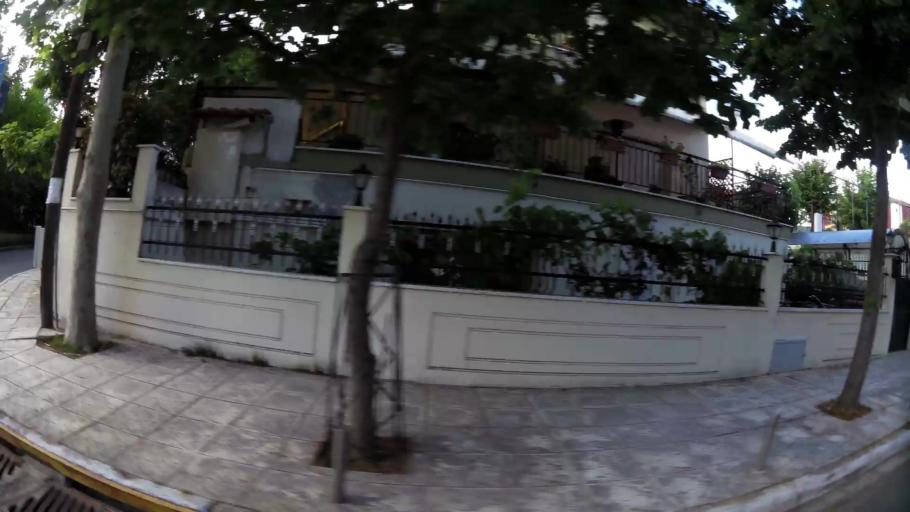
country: GR
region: Central Macedonia
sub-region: Nomos Thessalonikis
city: Pefka
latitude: 40.6554
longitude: 22.9897
